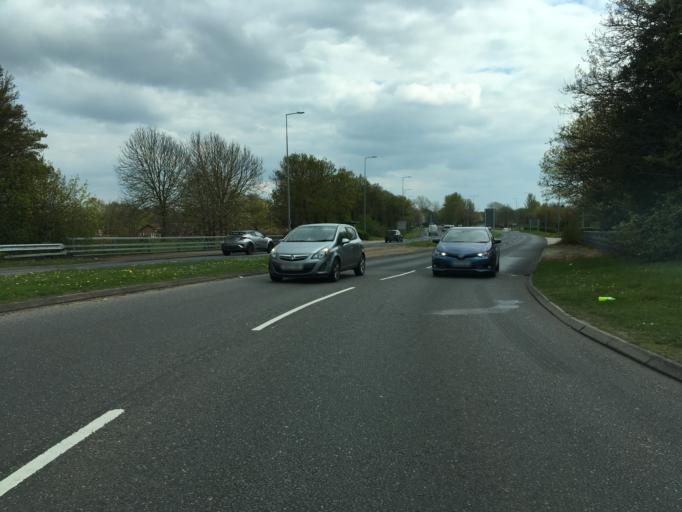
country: GB
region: England
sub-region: Milton Keynes
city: Milton Keynes
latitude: 52.0612
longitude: -0.7581
